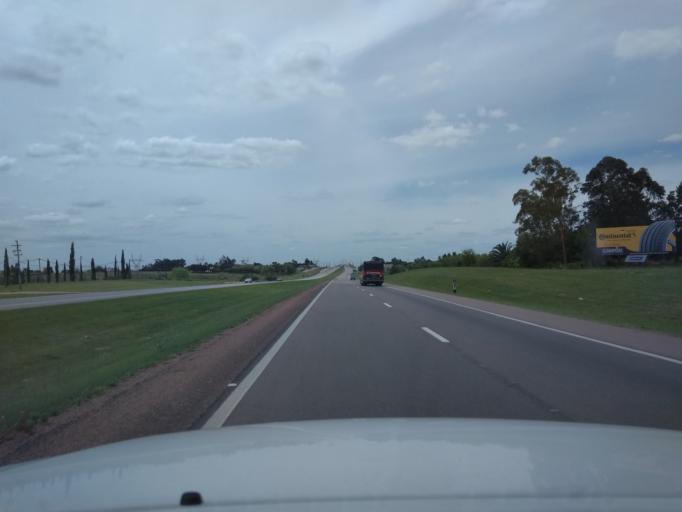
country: UY
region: Canelones
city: Las Piedras
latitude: -34.7315
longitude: -56.2489
